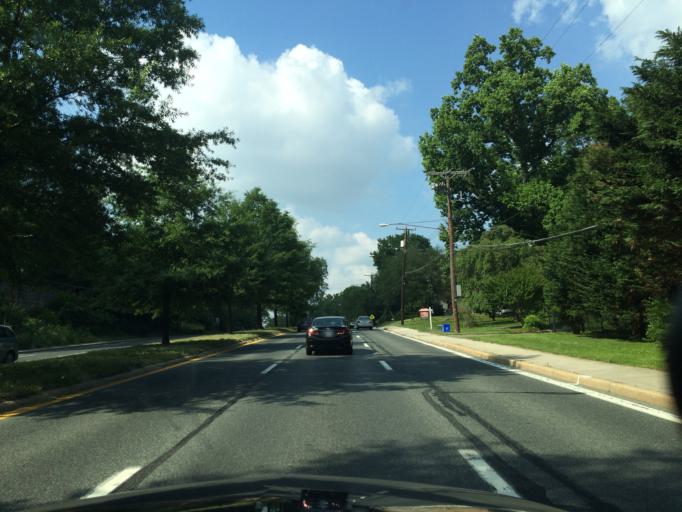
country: US
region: Maryland
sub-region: Montgomery County
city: South Kensington
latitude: 39.0133
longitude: -77.0798
